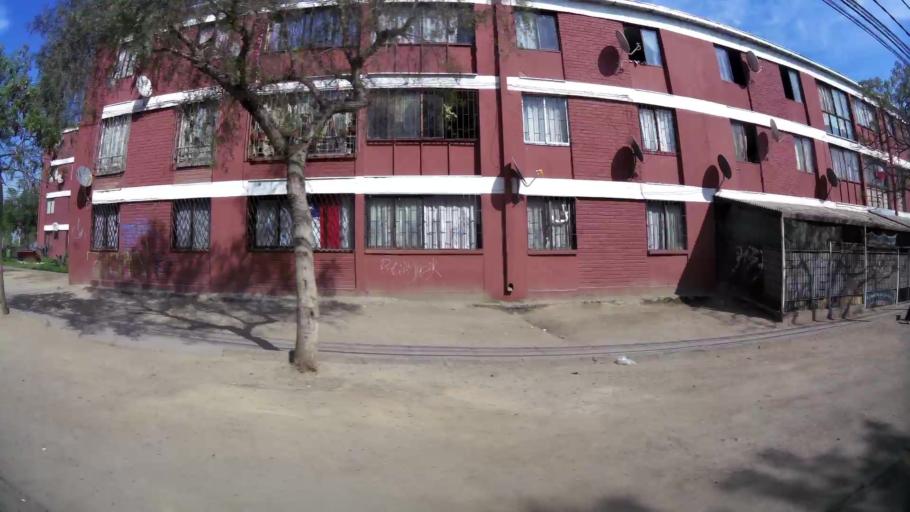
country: CL
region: Santiago Metropolitan
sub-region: Provincia de Santiago
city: Lo Prado
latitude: -33.4458
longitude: -70.7448
